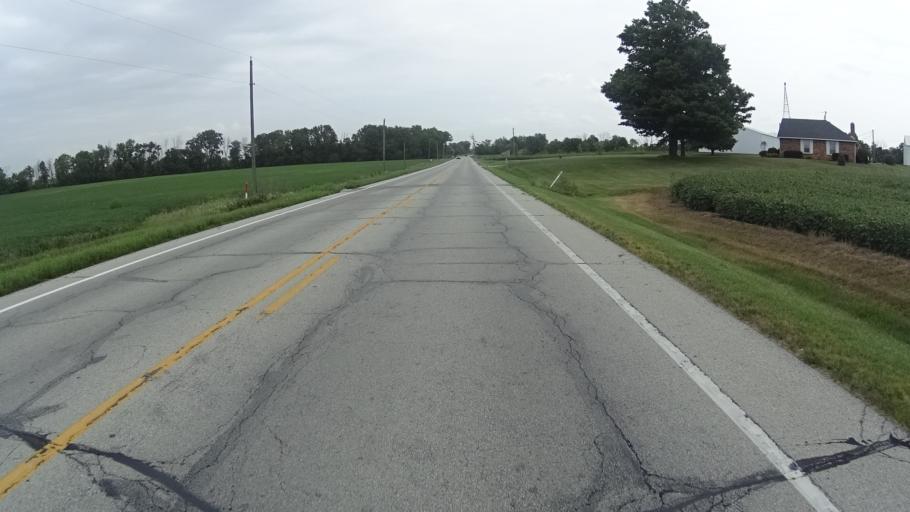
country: US
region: Indiana
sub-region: Madison County
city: Lapel
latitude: 40.0863
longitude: -85.8257
